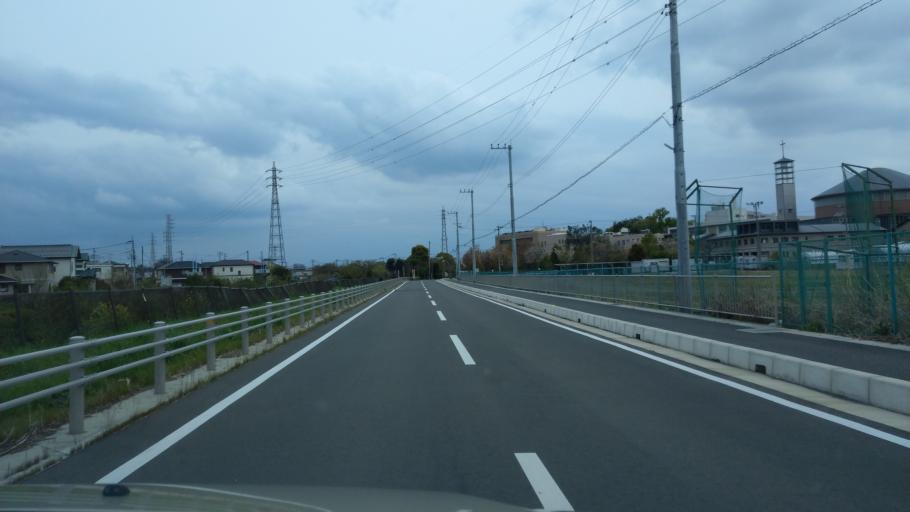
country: JP
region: Saitama
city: Ageoshimo
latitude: 35.9406
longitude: 139.5990
